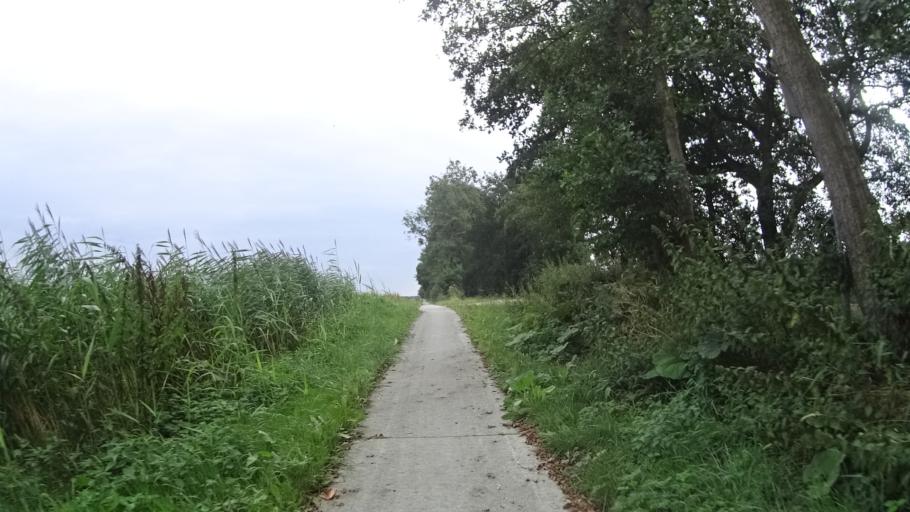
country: NL
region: Groningen
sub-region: Gemeente Slochteren
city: Slochteren
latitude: 53.2102
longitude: 6.8266
